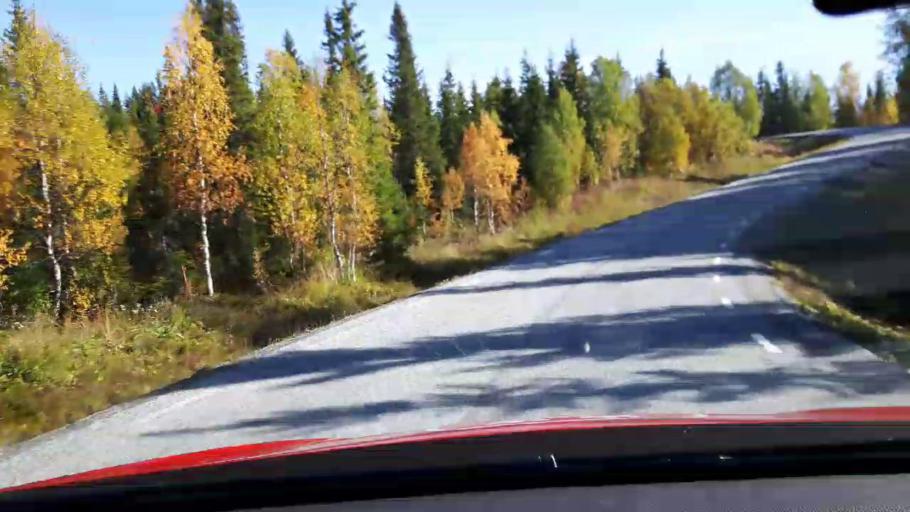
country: NO
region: Nord-Trondelag
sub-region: Royrvik
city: Royrvik
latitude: 64.8158
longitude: 14.1985
